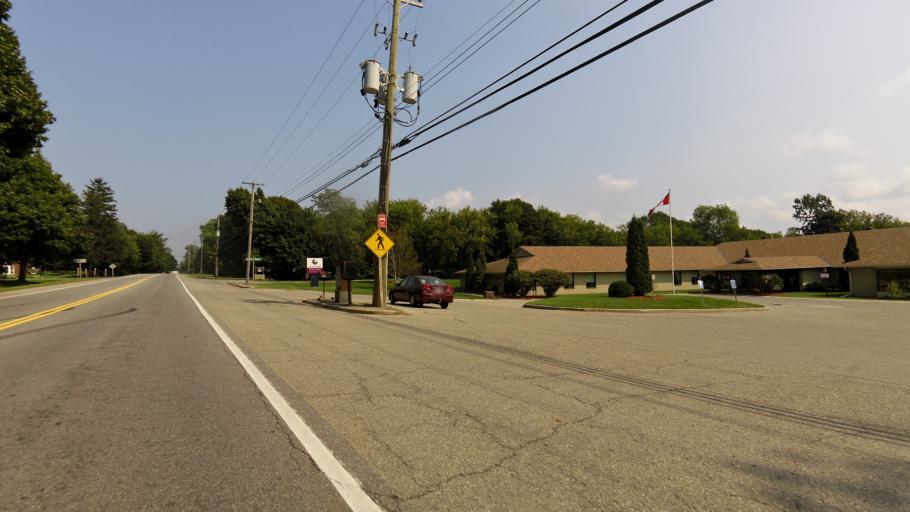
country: CA
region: Ontario
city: Brockville
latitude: 44.6038
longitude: -75.6631
